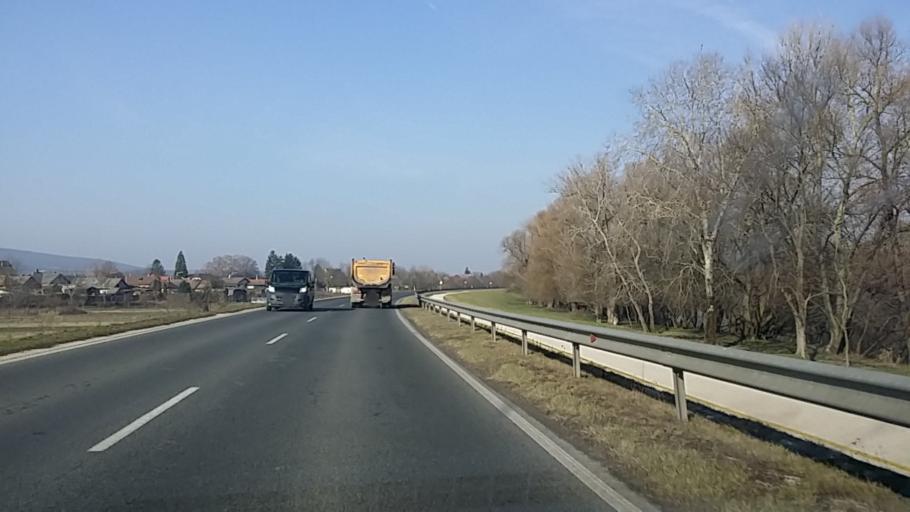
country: HU
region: Komarom-Esztergom
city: Tat
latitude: 47.7482
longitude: 18.6412
